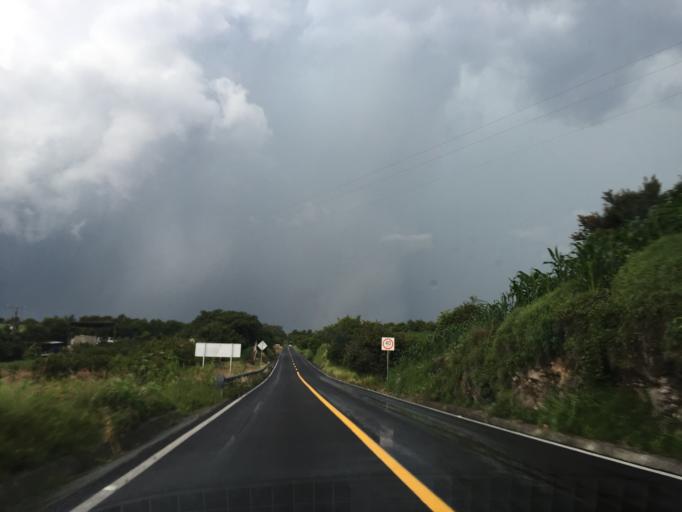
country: MX
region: Colima
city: Queseria
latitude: 19.3936
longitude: -103.5607
